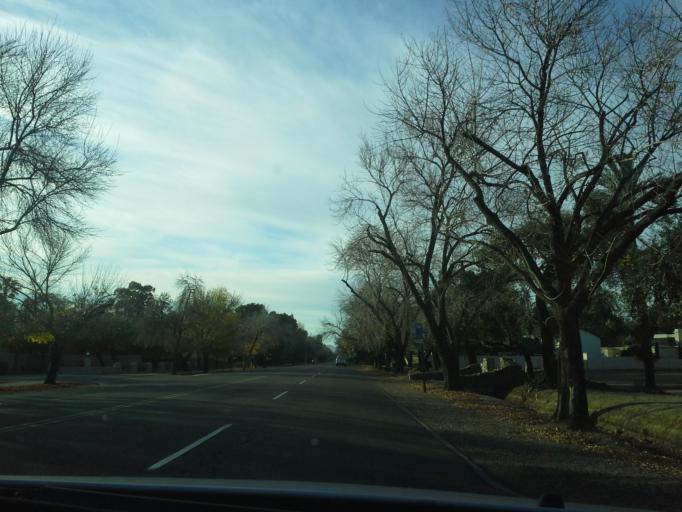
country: US
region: Arizona
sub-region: Maricopa County
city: Phoenix
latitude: 33.5492
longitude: -112.0739
